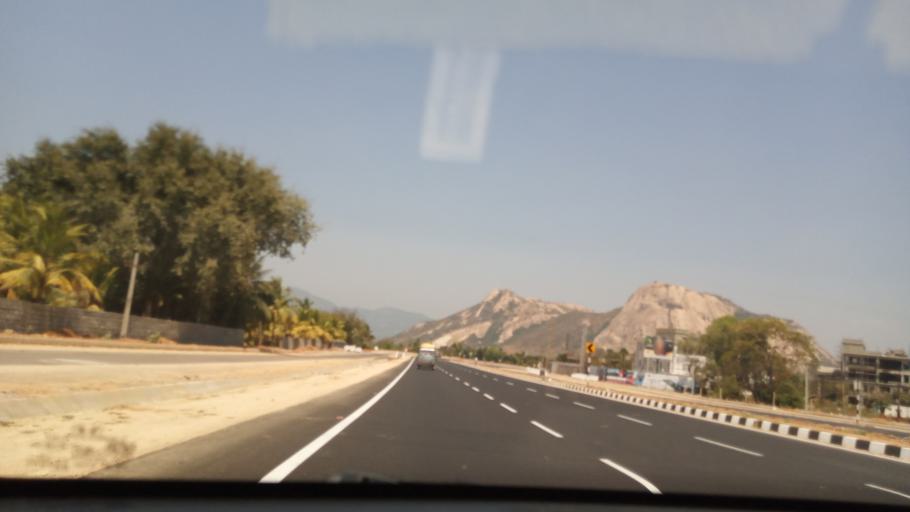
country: IN
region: Andhra Pradesh
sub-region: Chittoor
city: Narasingapuram
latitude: 13.5755
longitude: 79.2733
